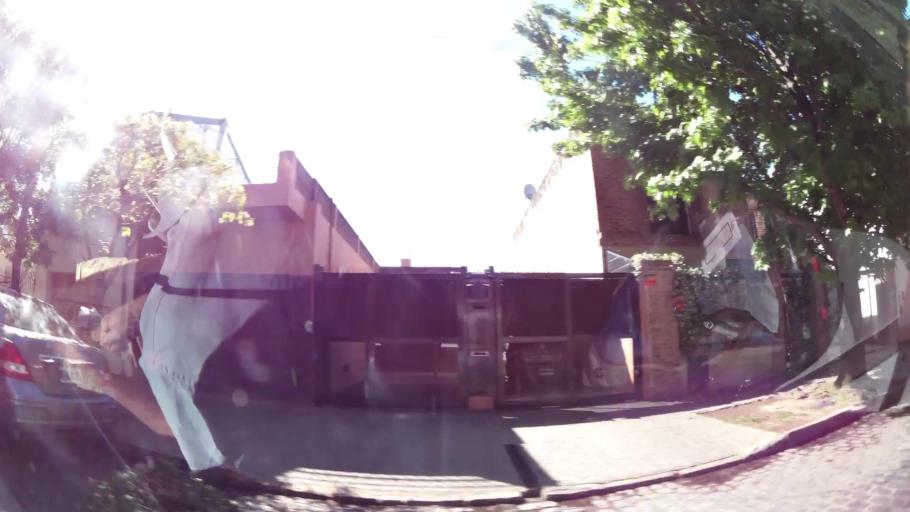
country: AR
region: Buenos Aires
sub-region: Partido de San Isidro
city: San Isidro
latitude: -34.4637
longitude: -58.5309
